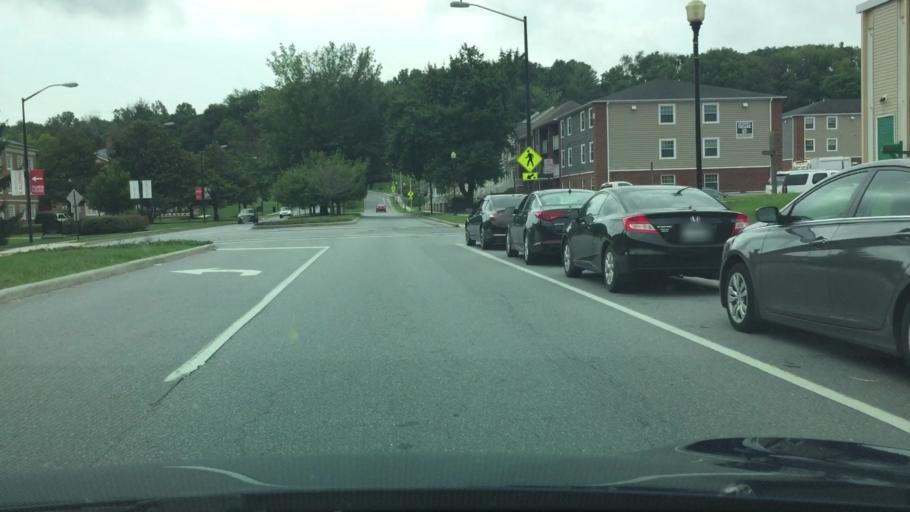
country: US
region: Virginia
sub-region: City of Radford
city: Radford
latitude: 37.1371
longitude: -80.5530
